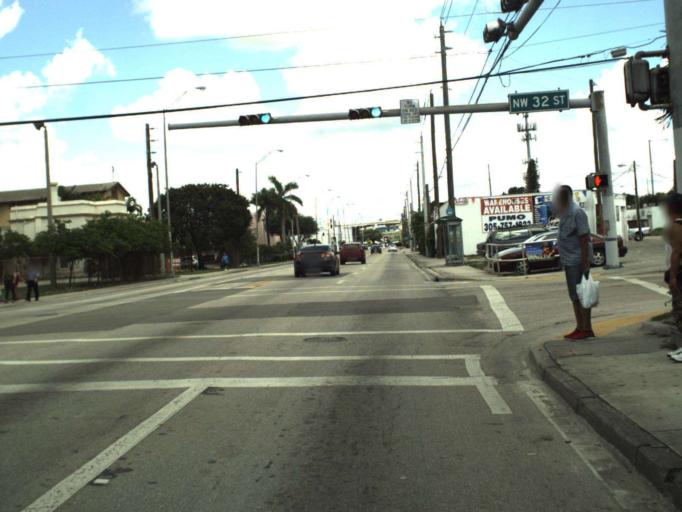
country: US
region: Florida
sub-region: Miami-Dade County
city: Allapattah
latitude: 25.8062
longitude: -80.2073
